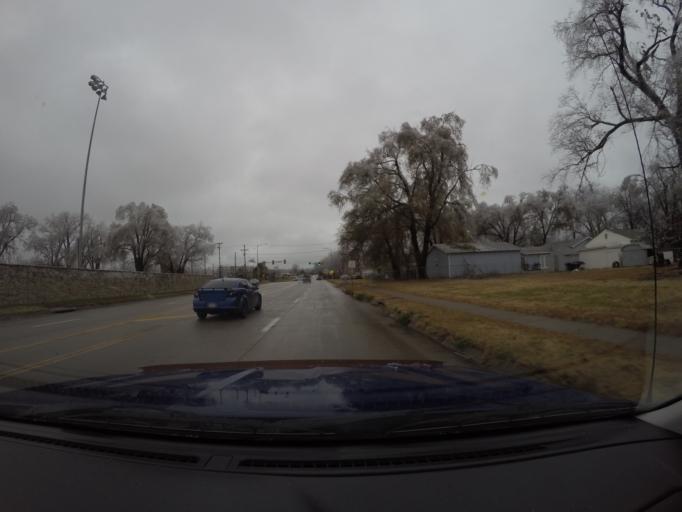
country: US
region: Kansas
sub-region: Riley County
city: Manhattan
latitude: 39.1743
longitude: -96.5754
